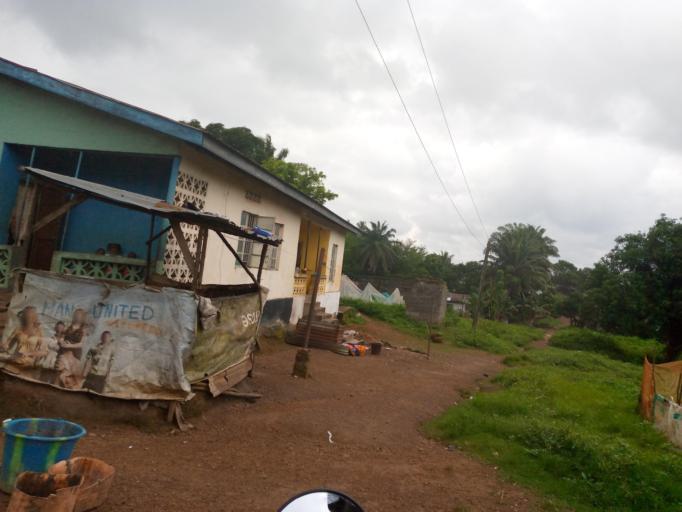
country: SL
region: Eastern Province
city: Kenema
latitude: 7.8611
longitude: -11.1944
